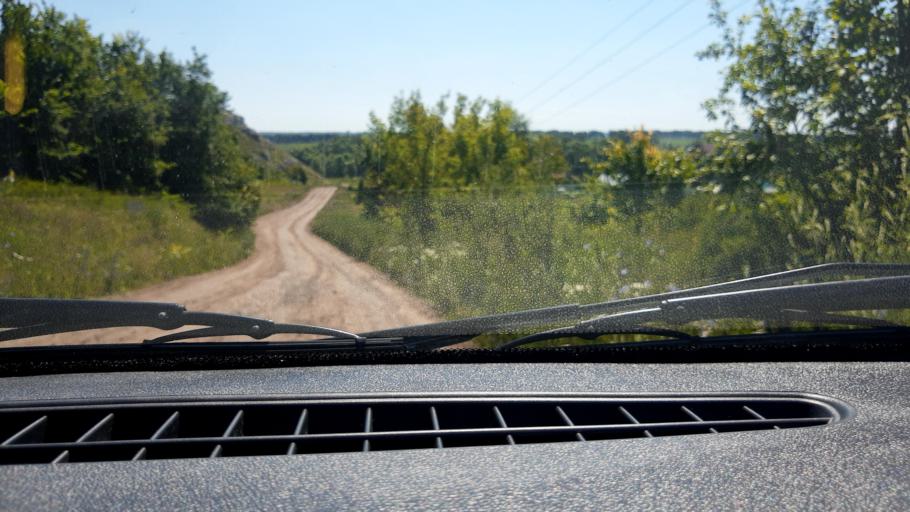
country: RU
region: Bashkortostan
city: Karmaskaly
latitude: 54.3610
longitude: 55.8958
